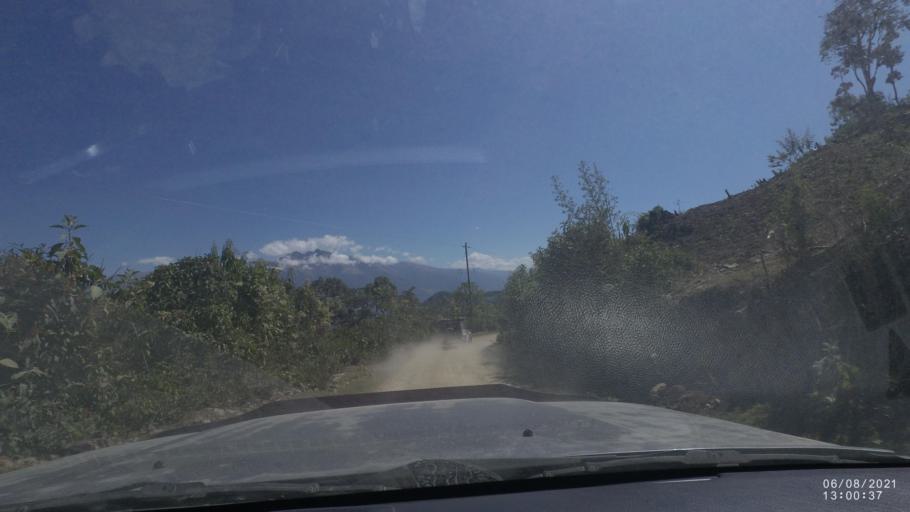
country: BO
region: Cochabamba
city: Colchani
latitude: -16.7476
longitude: -66.6898
